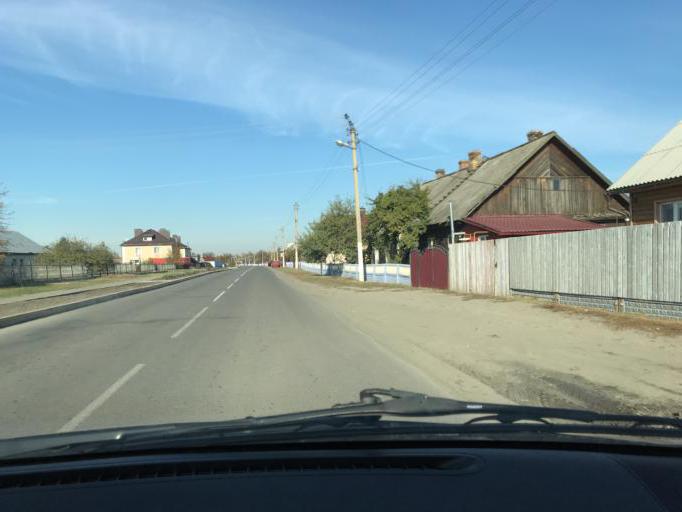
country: BY
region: Brest
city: Mikashevichy
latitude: 52.2281
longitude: 27.4589
